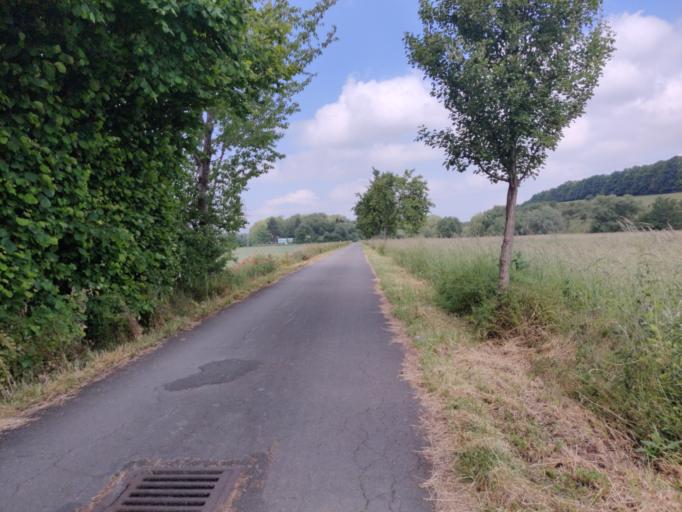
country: DE
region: Lower Saxony
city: Hildesheim
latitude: 52.1225
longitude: 9.9710
